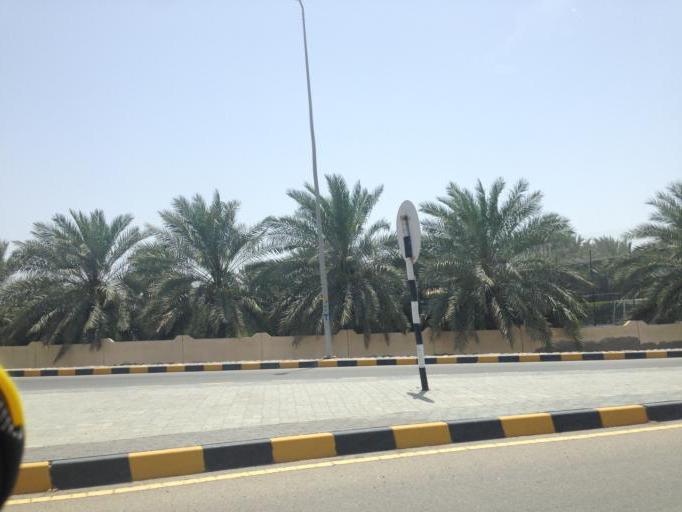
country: OM
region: Muhafazat Masqat
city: As Sib al Jadidah
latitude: 23.6792
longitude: 58.1381
